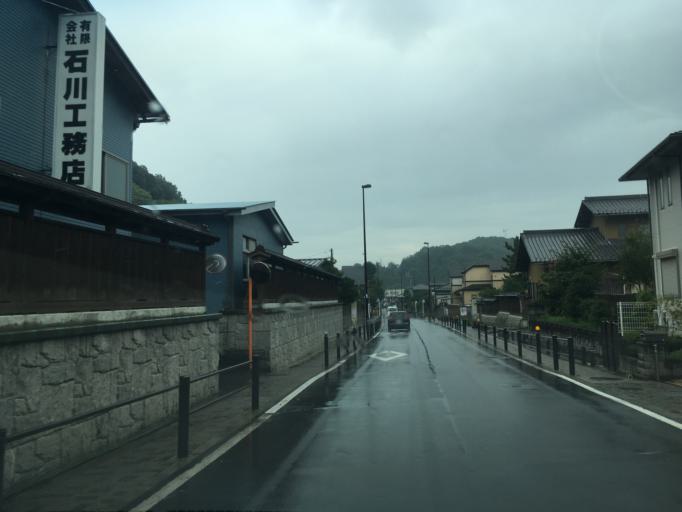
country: JP
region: Tokyo
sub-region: Machida-shi
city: Machida
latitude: 35.5998
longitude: 139.4372
